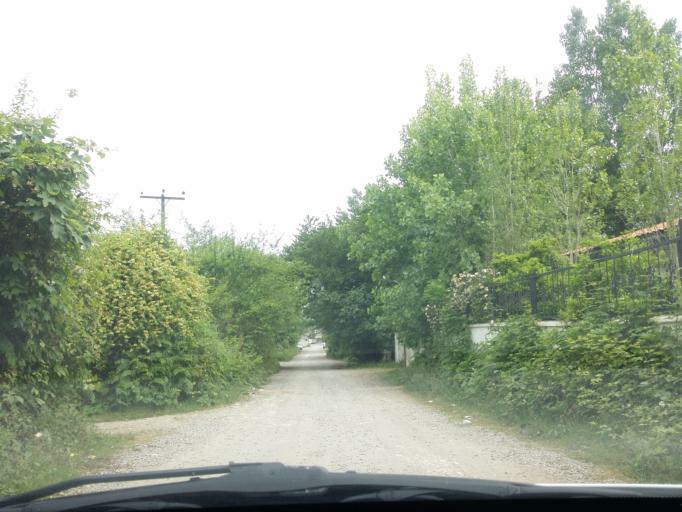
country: IR
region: Mazandaran
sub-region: Nowshahr
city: Nowshahr
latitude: 36.6211
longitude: 51.4943
